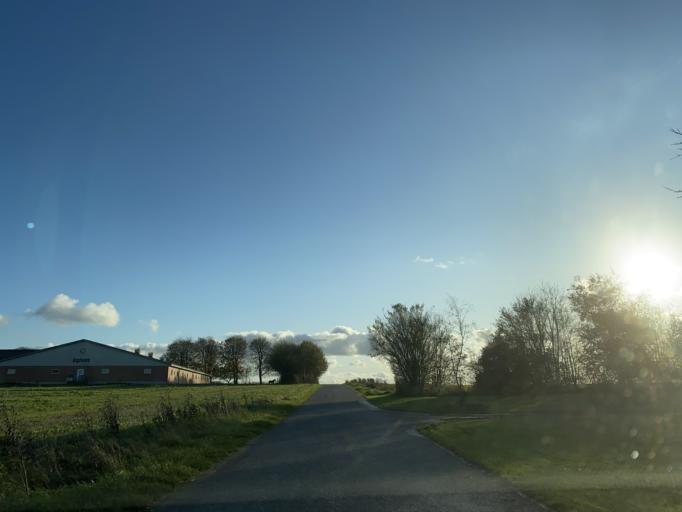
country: DK
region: Central Jutland
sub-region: Viborg Kommune
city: Bjerringbro
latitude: 56.3354
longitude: 9.7104
